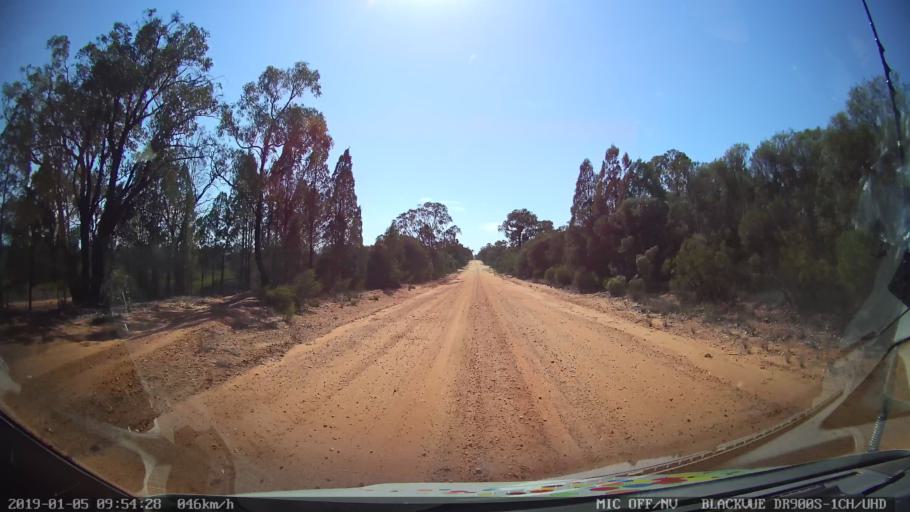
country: AU
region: New South Wales
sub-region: Gilgandra
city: Gilgandra
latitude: -31.6631
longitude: 148.7801
